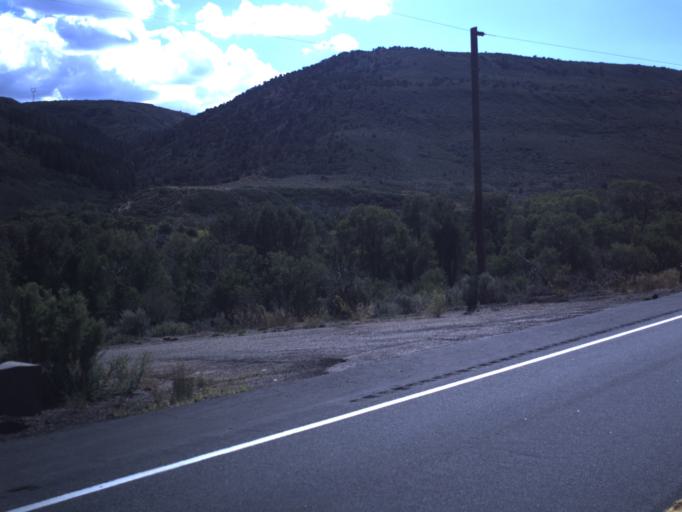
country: US
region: Utah
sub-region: Duchesne County
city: Duchesne
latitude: 40.1987
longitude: -110.8955
